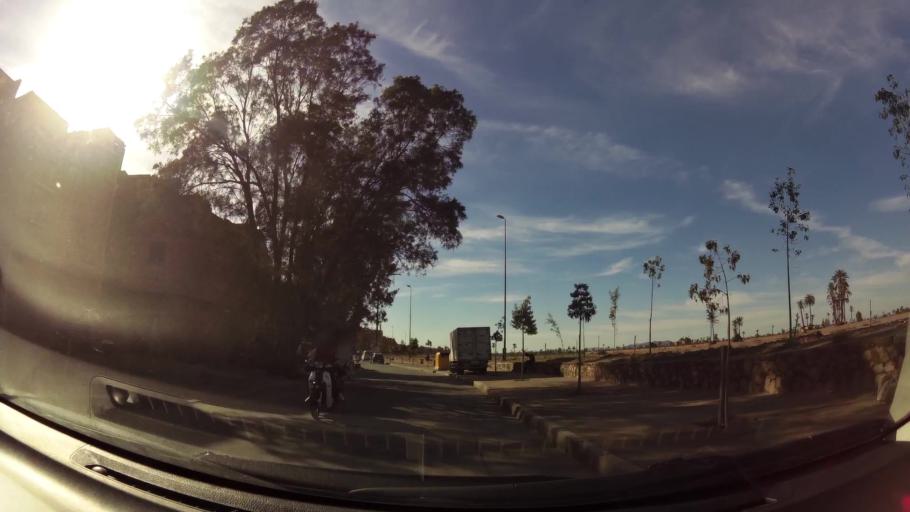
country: MA
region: Marrakech-Tensift-Al Haouz
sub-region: Marrakech
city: Marrakesh
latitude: 31.6146
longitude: -7.9608
